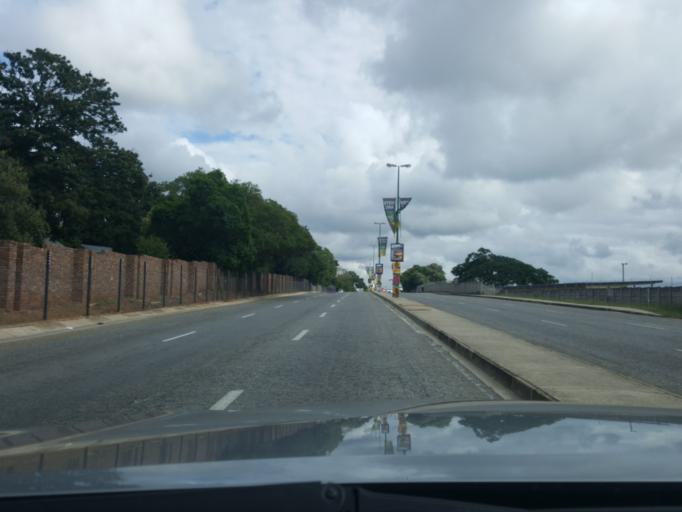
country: ZA
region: Mpumalanga
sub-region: Ehlanzeni District
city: Nelspruit
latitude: -25.4709
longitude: 30.9899
